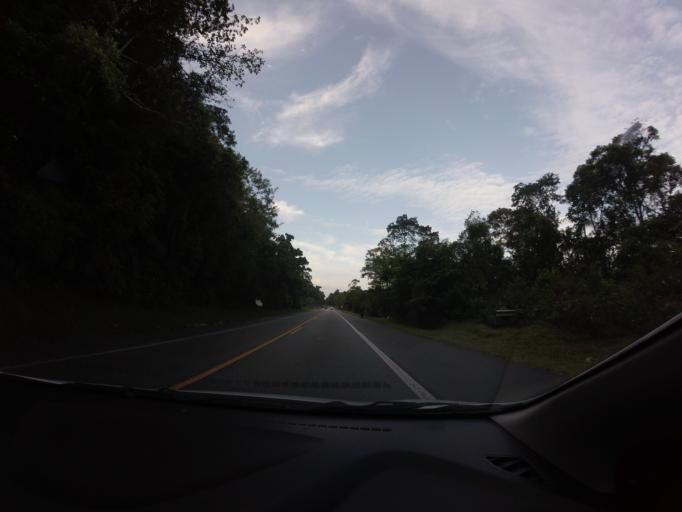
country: BR
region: Sao Paulo
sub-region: Bertioga
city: Bertioga
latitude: -23.8684
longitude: -46.1712
